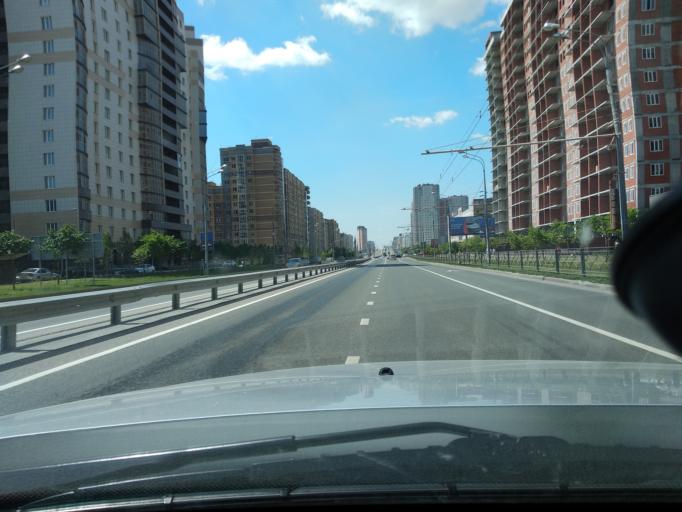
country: RU
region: Tatarstan
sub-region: Gorod Kazan'
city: Kazan
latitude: 55.8194
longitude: 49.1456
